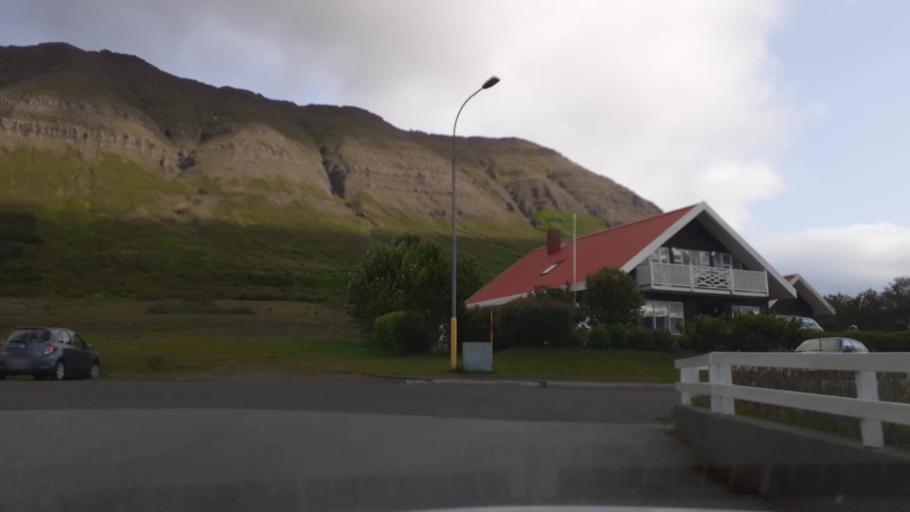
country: IS
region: East
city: Neskaupstadur
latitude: 65.1492
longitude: -13.6749
